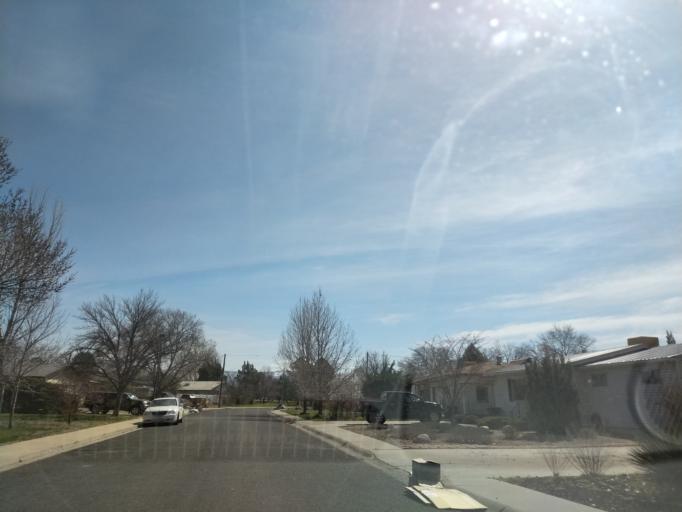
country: US
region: Colorado
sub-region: Mesa County
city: Grand Junction
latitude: 39.0819
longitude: -108.5699
